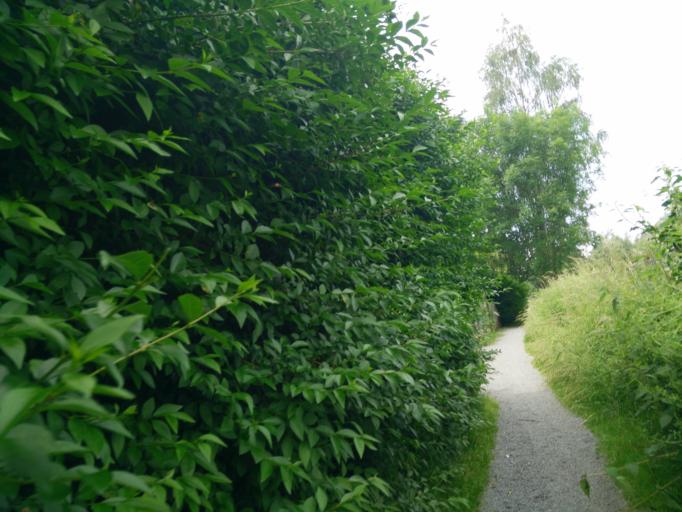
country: BE
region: Flanders
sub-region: Provincie Vlaams-Brabant
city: Halle
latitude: 50.7420
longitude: 4.2651
